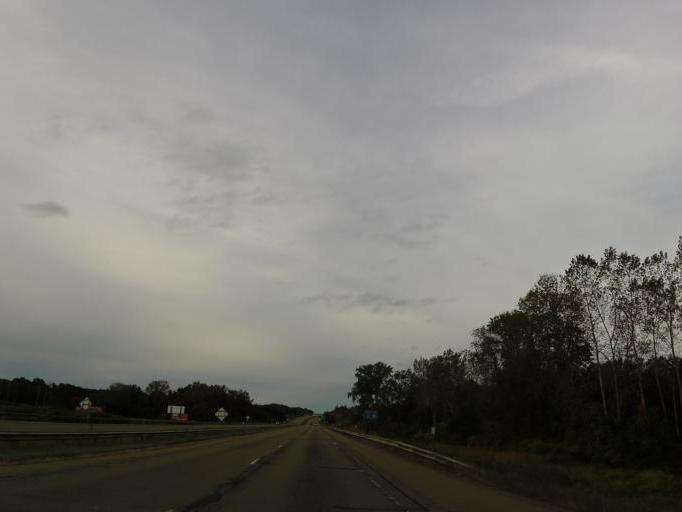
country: US
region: New York
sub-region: Chautauqua County
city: Silver Creek
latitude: 42.5588
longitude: -79.0991
